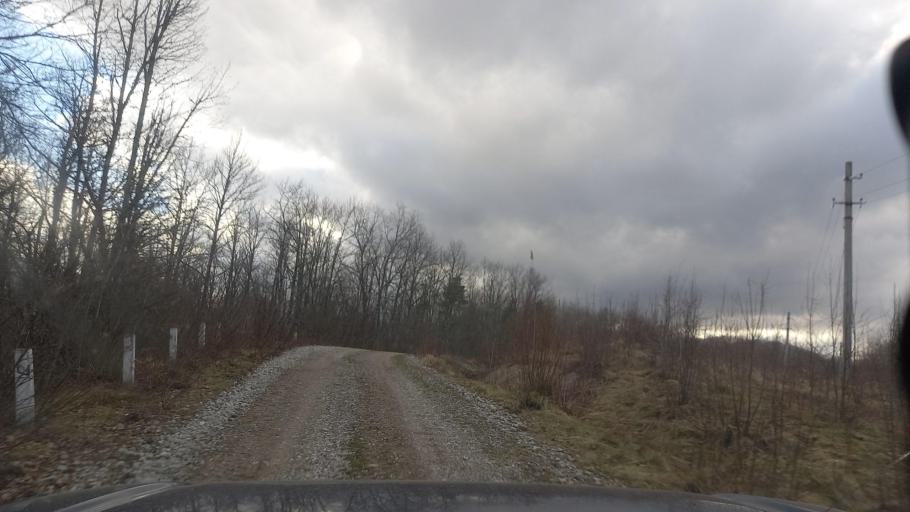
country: RU
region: Krasnodarskiy
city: Smolenskaya
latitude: 44.5729
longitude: 38.7991
